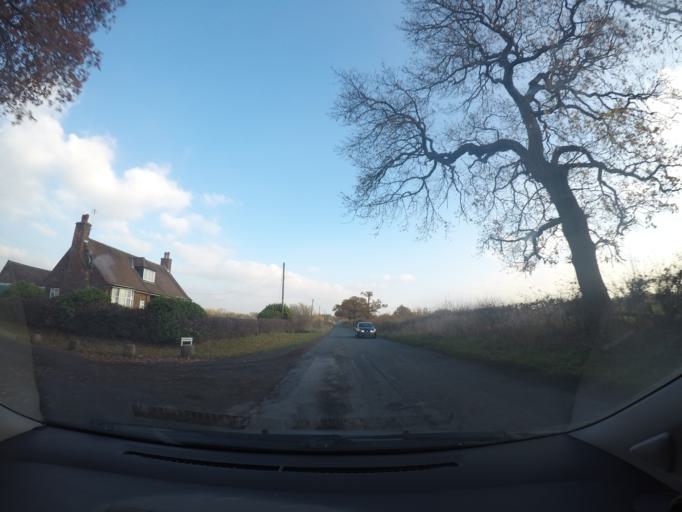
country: GB
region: England
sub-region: City of York
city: Huntington
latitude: 53.9996
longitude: -1.0352
